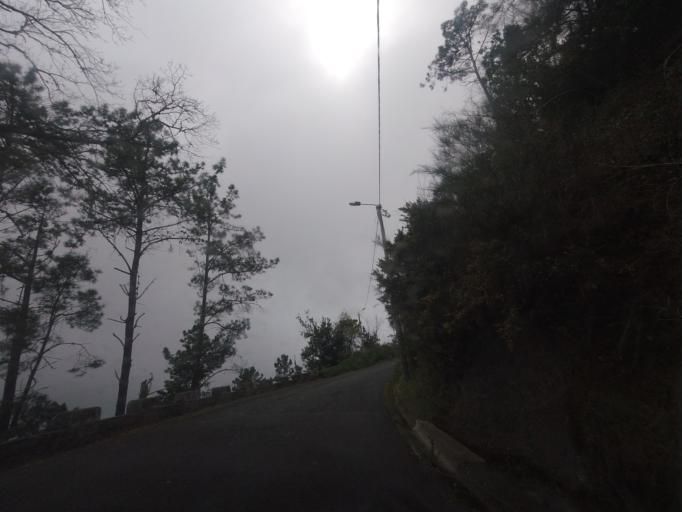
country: PT
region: Madeira
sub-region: Calheta
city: Faja da Ovelha
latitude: 32.7680
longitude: -17.2118
